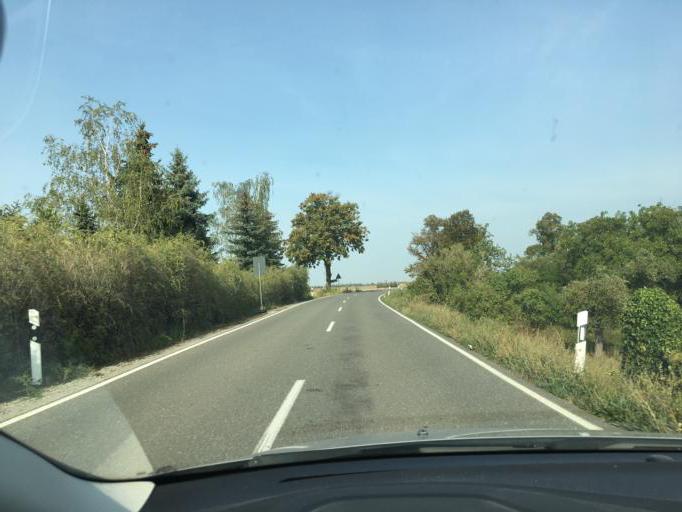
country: DE
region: Saxony-Anhalt
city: Nienburg/Saale
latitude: 51.8450
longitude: 11.7795
